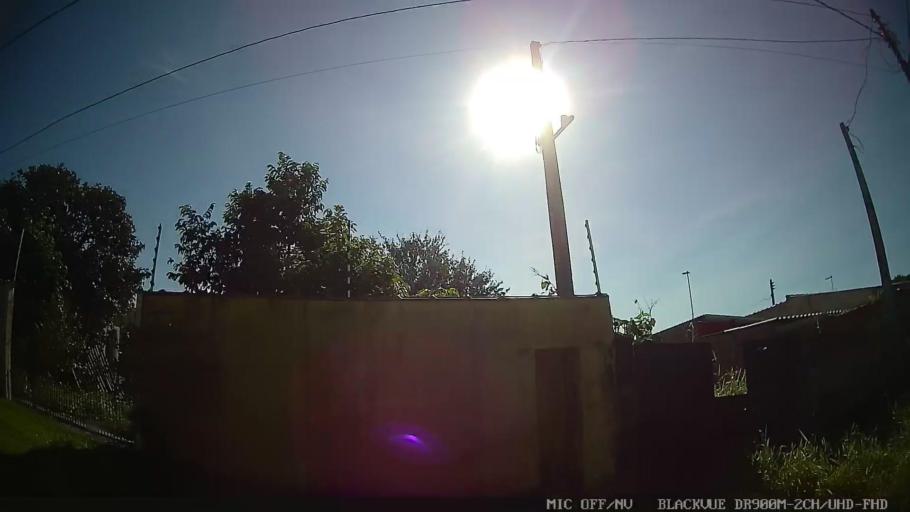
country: BR
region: Sao Paulo
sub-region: Itanhaem
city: Itanhaem
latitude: -24.2215
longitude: -46.8783
